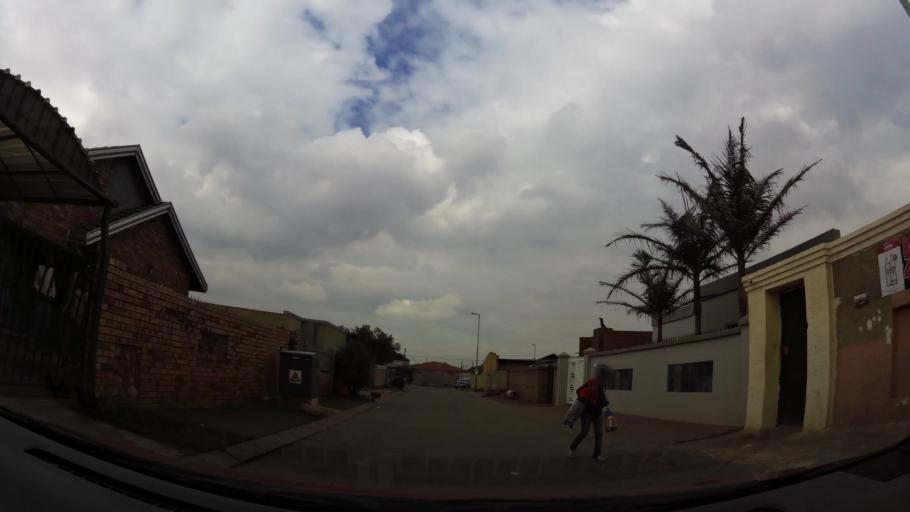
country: ZA
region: Gauteng
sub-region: City of Johannesburg Metropolitan Municipality
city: Soweto
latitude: -26.2633
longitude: 27.8315
